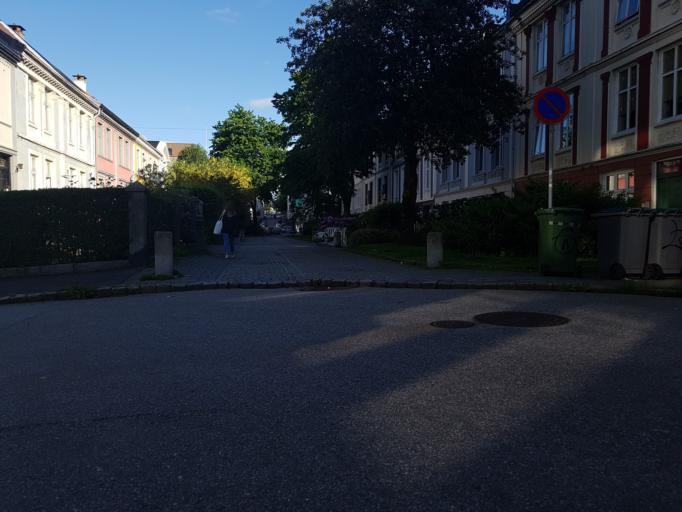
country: NO
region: Hordaland
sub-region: Bergen
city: Bergen
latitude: 60.3870
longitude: 5.3278
